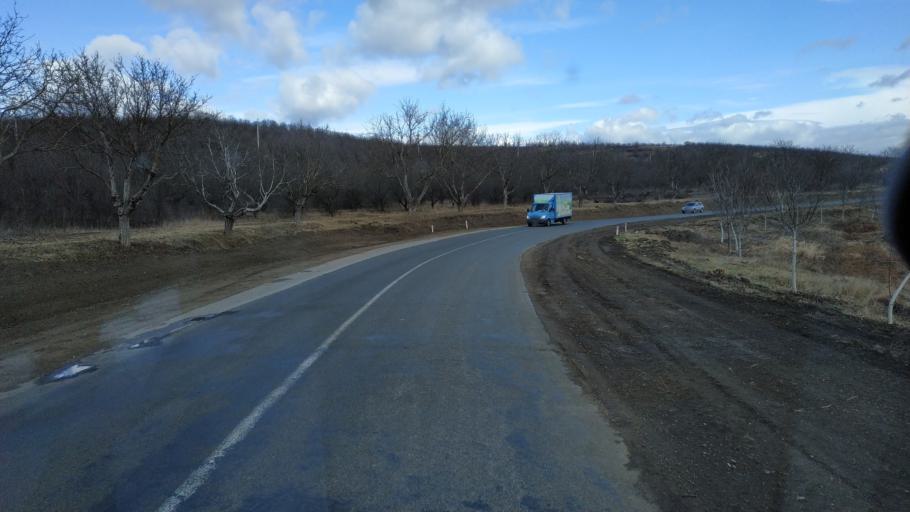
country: MD
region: Stinga Nistrului
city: Bucovat
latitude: 47.1689
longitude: 28.4408
